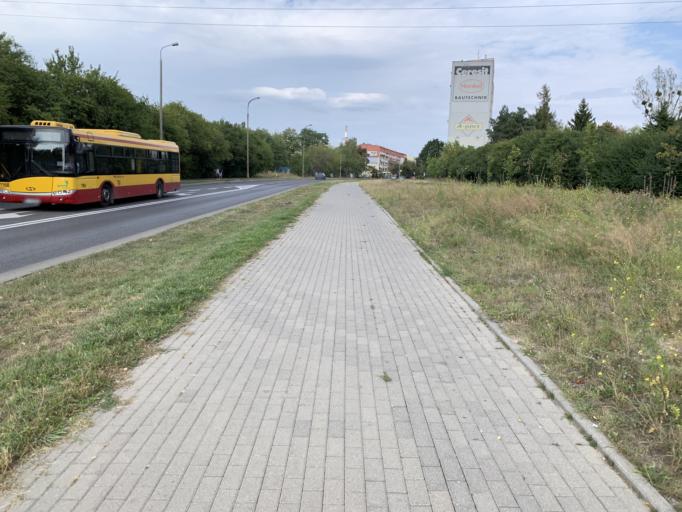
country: PL
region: Lodz Voivodeship
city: Lodz
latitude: 51.7818
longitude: 19.4266
